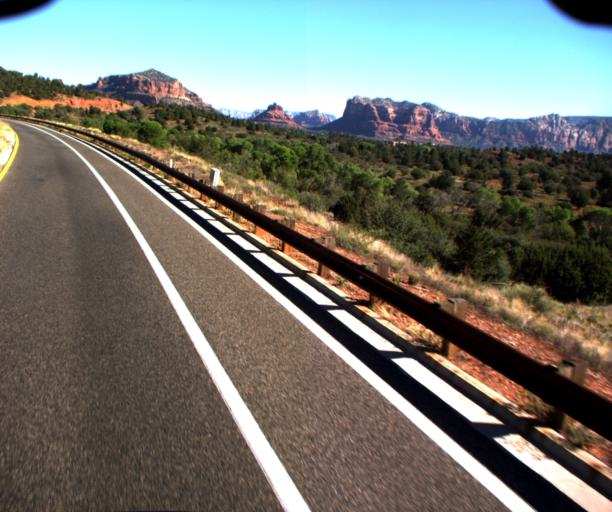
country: US
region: Arizona
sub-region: Yavapai County
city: Big Park
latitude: 34.7574
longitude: -111.7651
